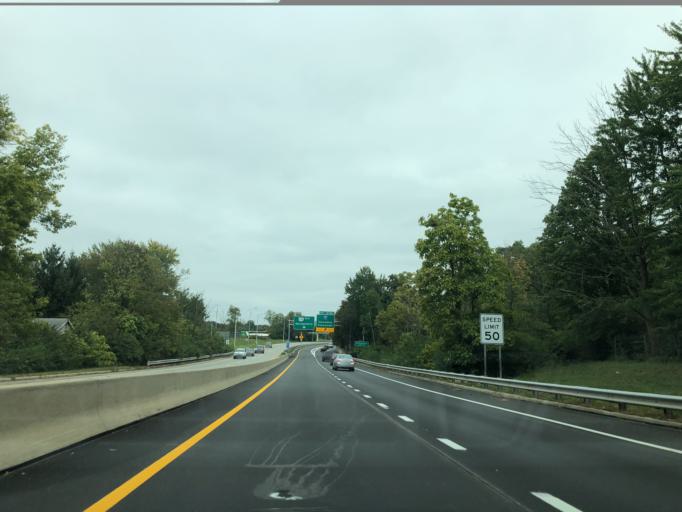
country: US
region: Ohio
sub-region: Hamilton County
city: Blue Ash
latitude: 39.2259
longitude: -84.3742
